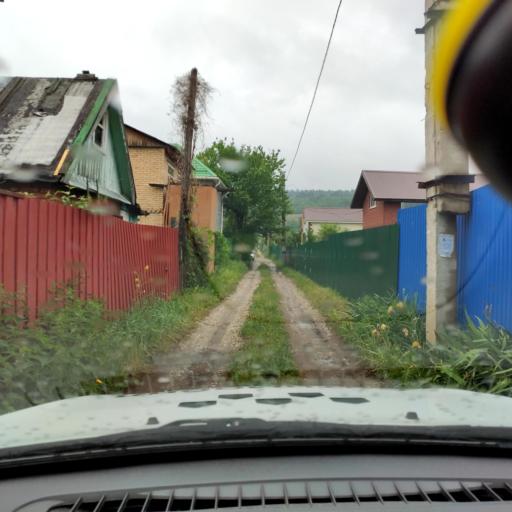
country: RU
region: Samara
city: Povolzhskiy
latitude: 53.4642
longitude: 49.6520
